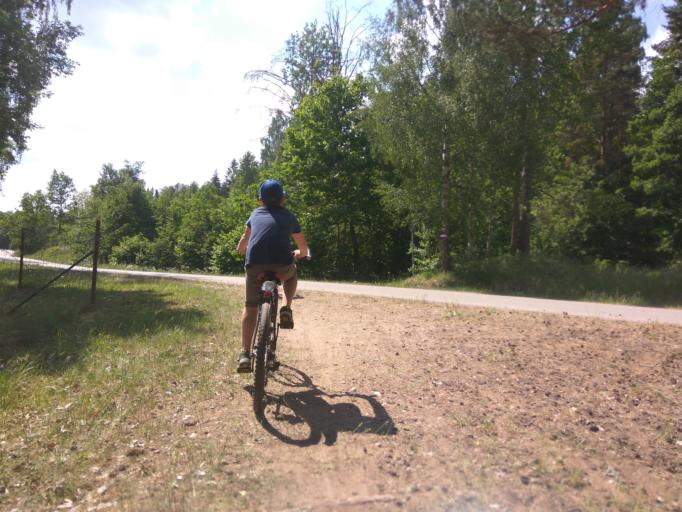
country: LV
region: Kuldigas Rajons
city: Kuldiga
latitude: 56.9178
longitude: 21.9646
